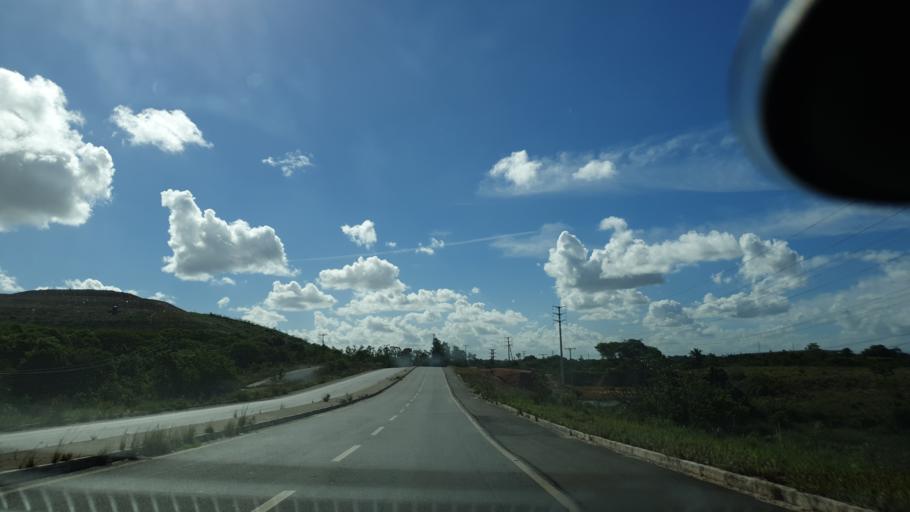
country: BR
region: Bahia
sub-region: Camacari
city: Camacari
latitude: -12.6852
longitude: -38.2560
